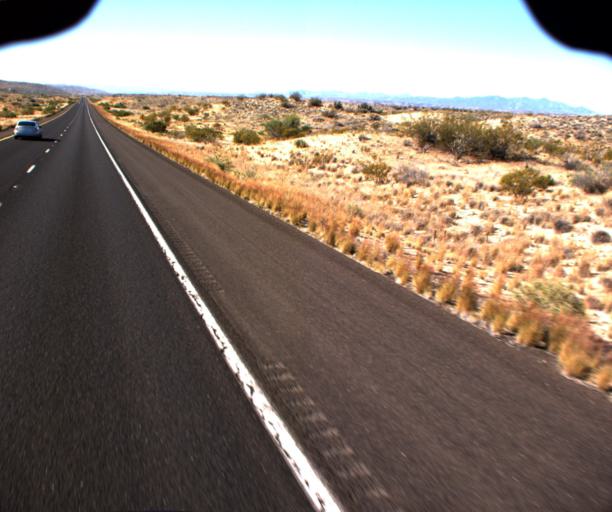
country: US
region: Arizona
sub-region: Mohave County
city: Kingman
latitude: 35.0643
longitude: -113.6657
